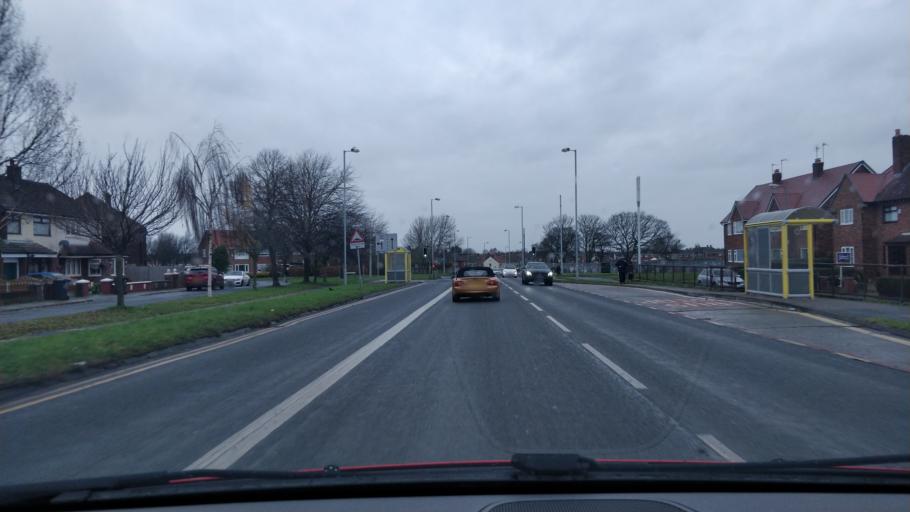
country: GB
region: England
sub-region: Sefton
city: Litherland
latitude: 53.4793
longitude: -2.9962
